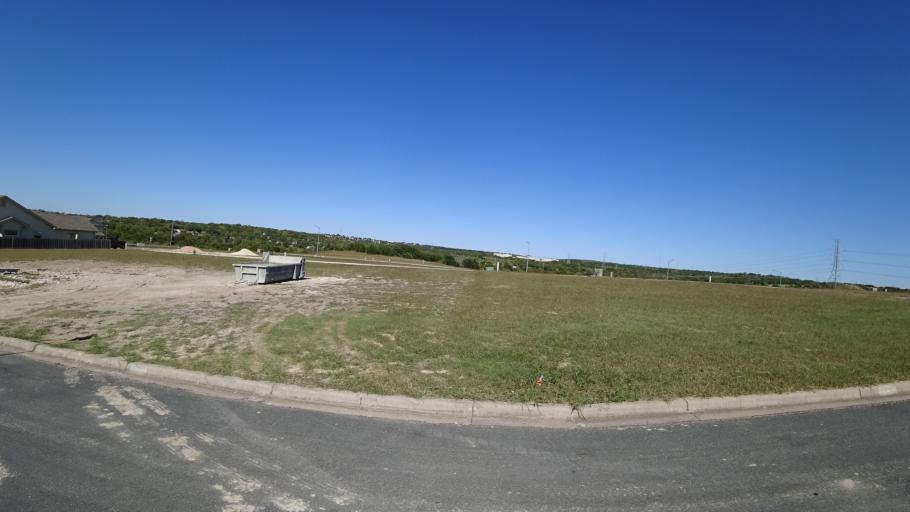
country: US
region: Texas
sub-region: Travis County
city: Hornsby Bend
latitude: 30.2935
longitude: -97.6418
